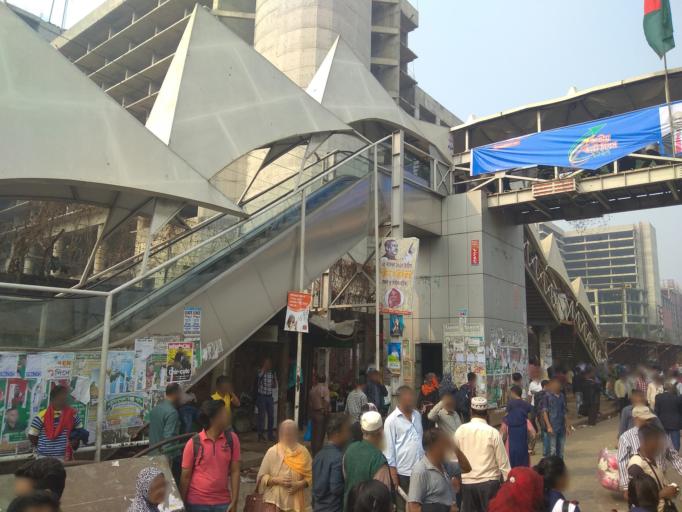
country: BD
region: Dhaka
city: Tungi
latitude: 23.8507
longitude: 90.4081
